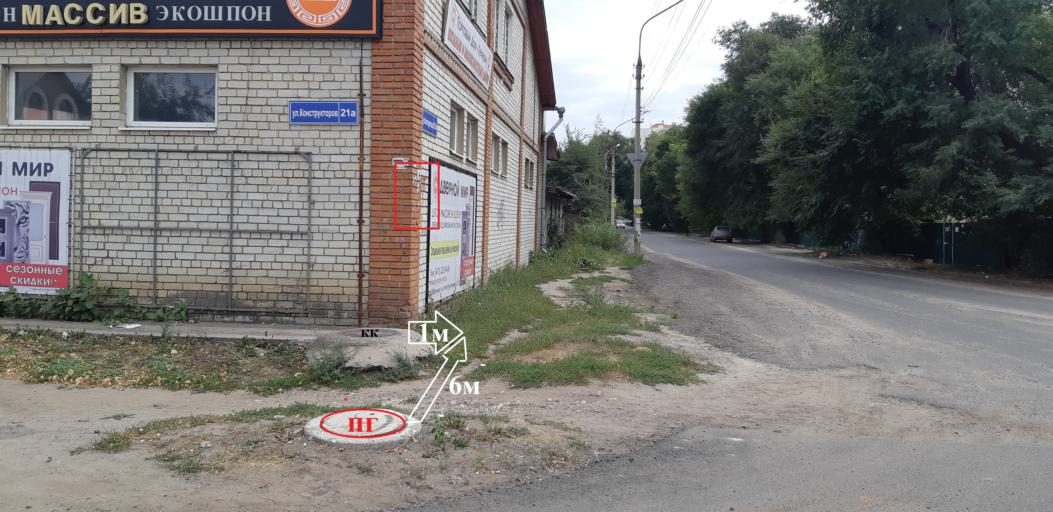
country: RU
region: Voronezj
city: Voronezh
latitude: 51.6646
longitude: 39.1670
